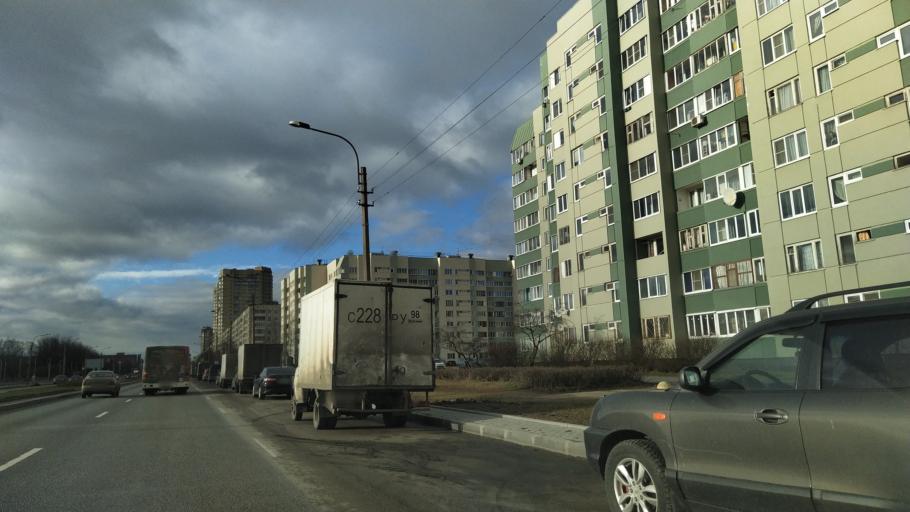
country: RU
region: St.-Petersburg
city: Grazhdanka
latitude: 60.0327
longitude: 30.3837
